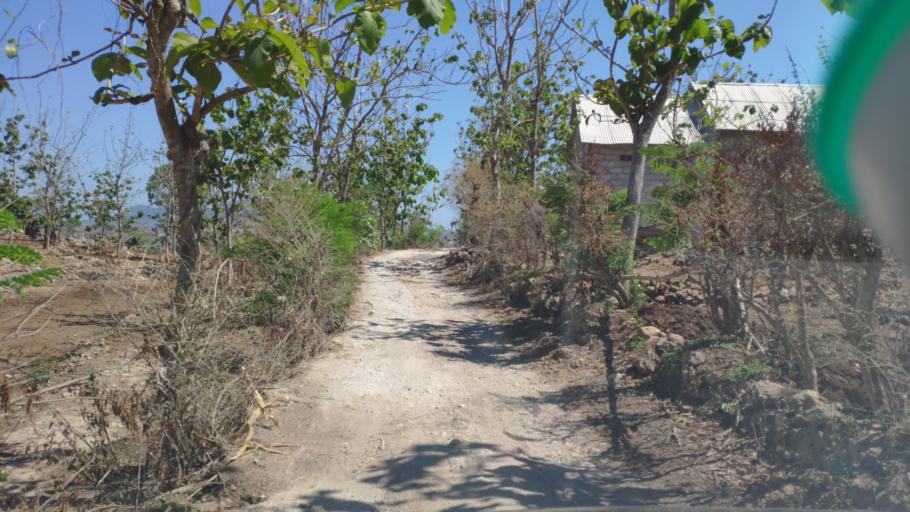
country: ID
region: Central Java
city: Jurangjero
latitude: -6.8935
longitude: 111.5106
